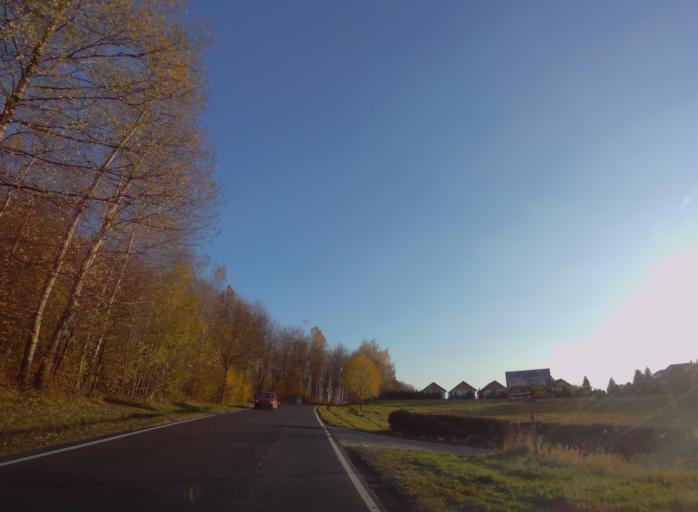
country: PL
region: Subcarpathian Voivodeship
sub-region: Powiat leski
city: Polanczyk
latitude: 49.3877
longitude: 22.4308
